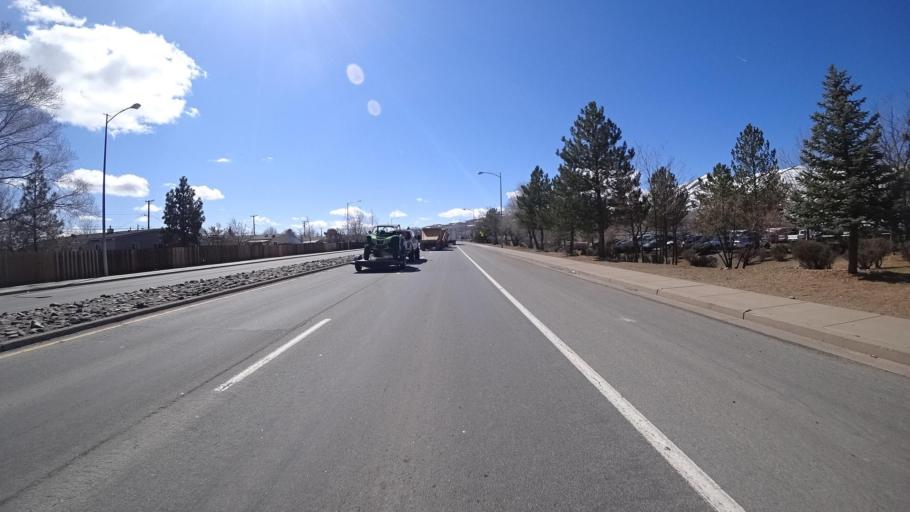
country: US
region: Nevada
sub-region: Washoe County
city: Lemmon Valley
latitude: 39.6329
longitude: -119.8820
